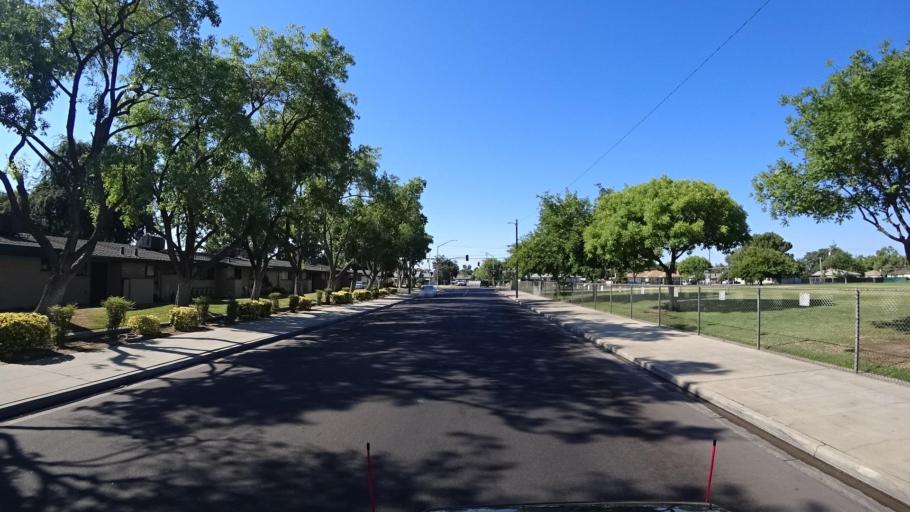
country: US
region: California
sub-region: Fresno County
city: Fresno
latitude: 36.7877
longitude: -119.7589
